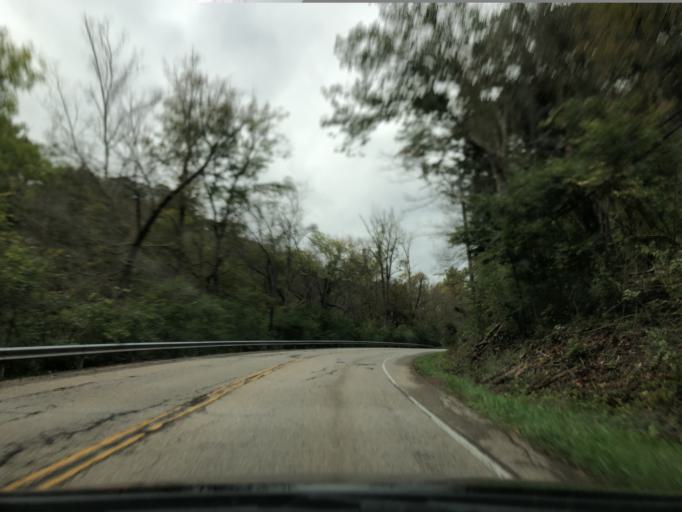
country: US
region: Ohio
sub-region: Hamilton County
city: Madeira
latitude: 39.1770
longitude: -84.3754
